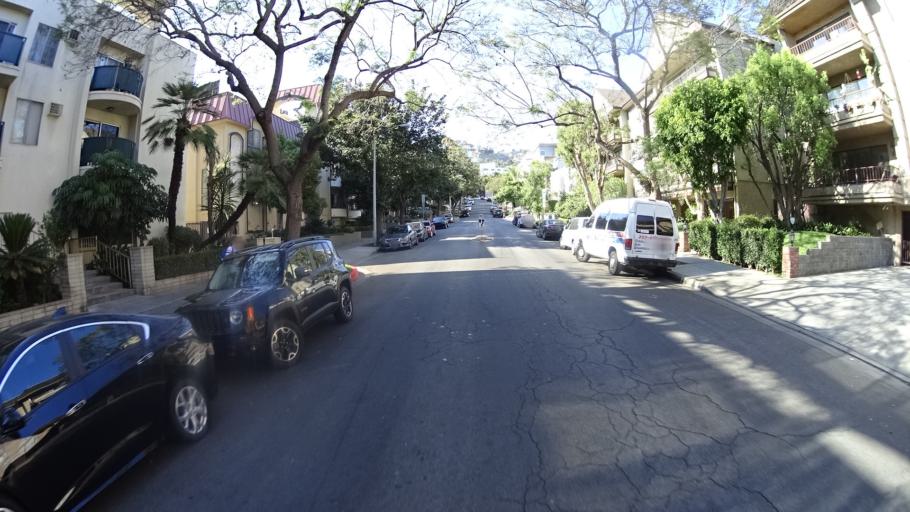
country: US
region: California
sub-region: Los Angeles County
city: West Hollywood
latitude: 34.0917
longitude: -118.3728
